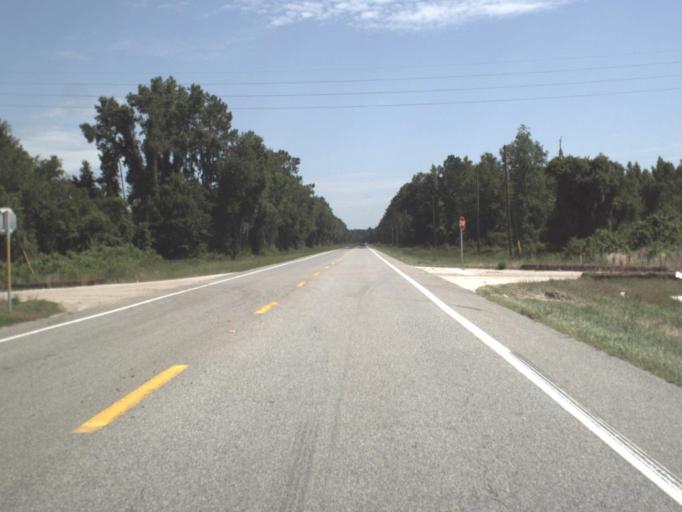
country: US
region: Florida
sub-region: Hamilton County
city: Jasper
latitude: 30.4634
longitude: -82.9314
